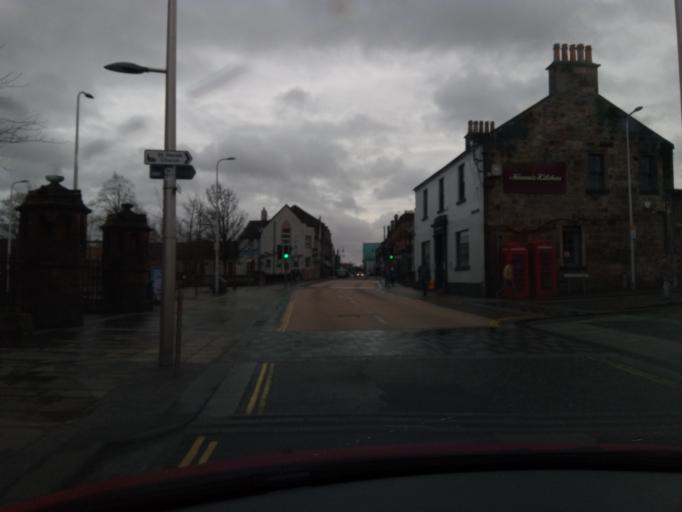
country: GB
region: Scotland
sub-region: East Dunbartonshire
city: Kirkintilloch
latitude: 55.9389
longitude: -4.1556
